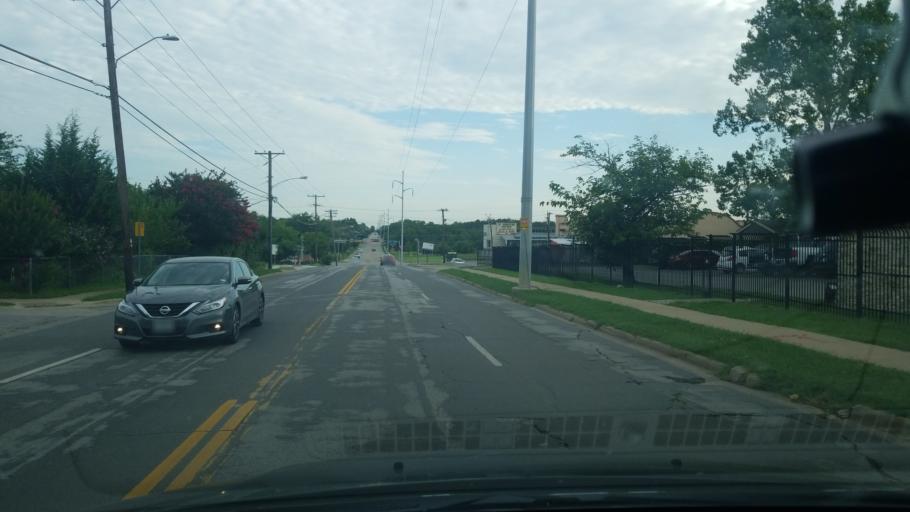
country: US
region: Texas
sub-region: Dallas County
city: Balch Springs
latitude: 32.7325
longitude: -96.6569
